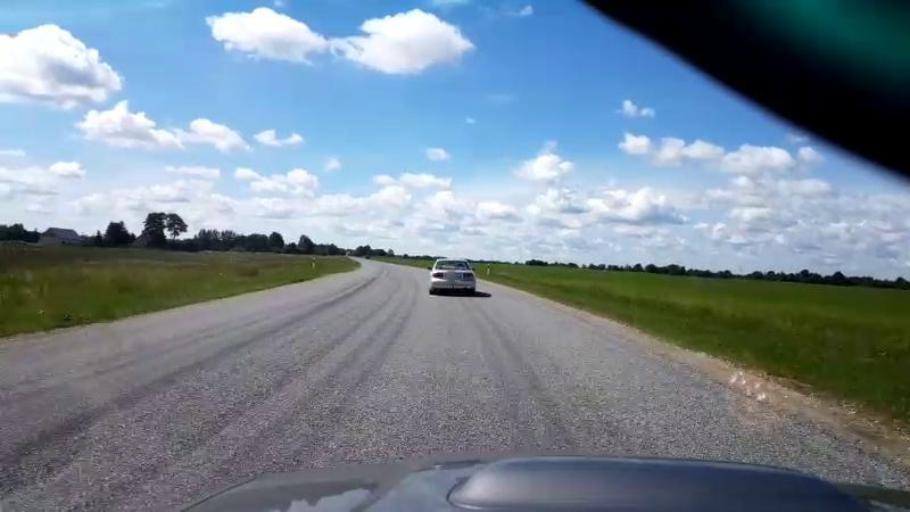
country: EE
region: Laeaene-Virumaa
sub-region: Tapa vald
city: Tapa
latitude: 59.2209
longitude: 25.8881
